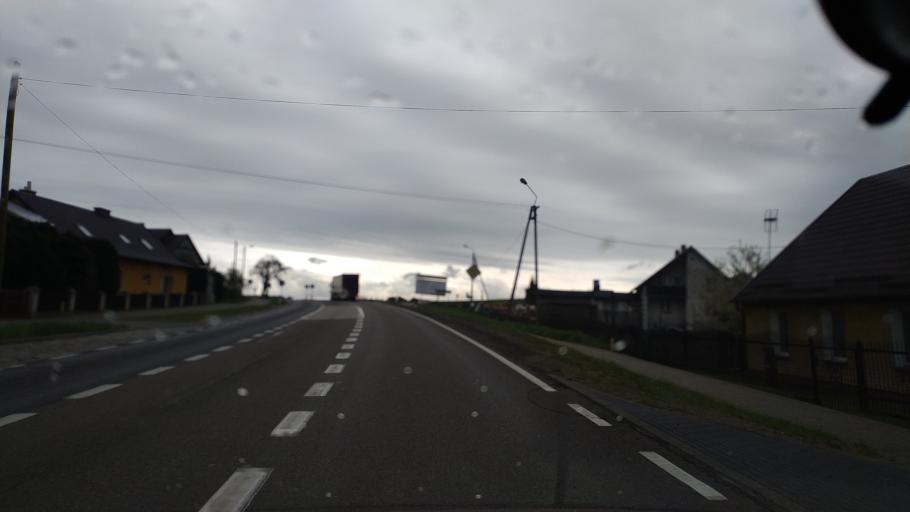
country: PL
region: Pomeranian Voivodeship
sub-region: Powiat starogardzki
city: Kaliska
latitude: 53.8876
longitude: 18.2149
